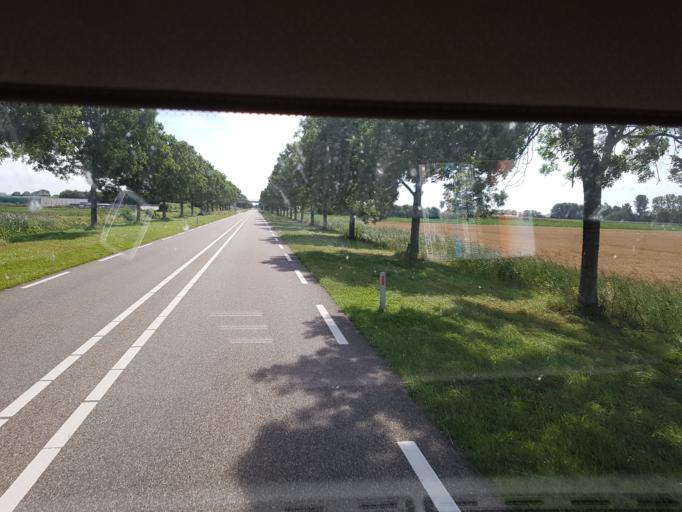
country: NL
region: North Brabant
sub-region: Gemeente Aalburg
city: Aalburg
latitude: 51.7708
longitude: 5.0687
